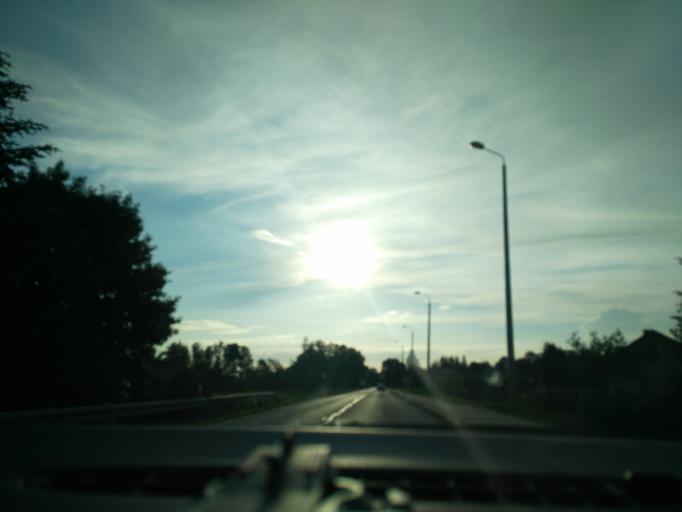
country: PL
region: Lublin Voivodeship
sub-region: Powiat krasnicki
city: Krasnik
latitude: 50.9098
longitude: 22.2598
